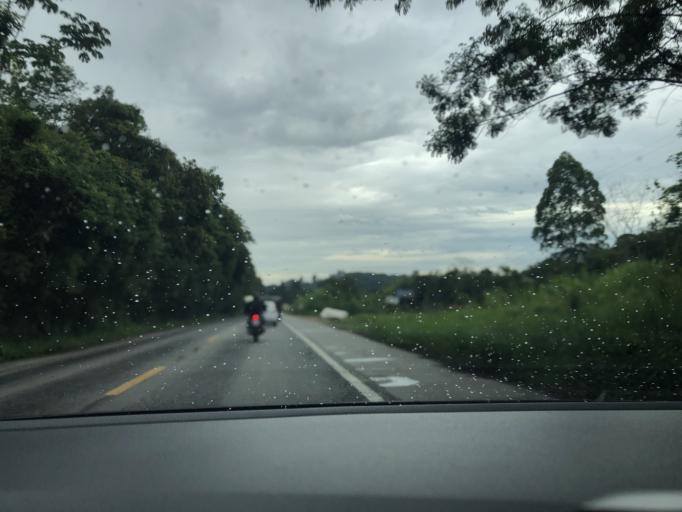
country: BR
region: Sao Paulo
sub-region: Jarinu
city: Jarinu
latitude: -23.1200
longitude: -46.7301
